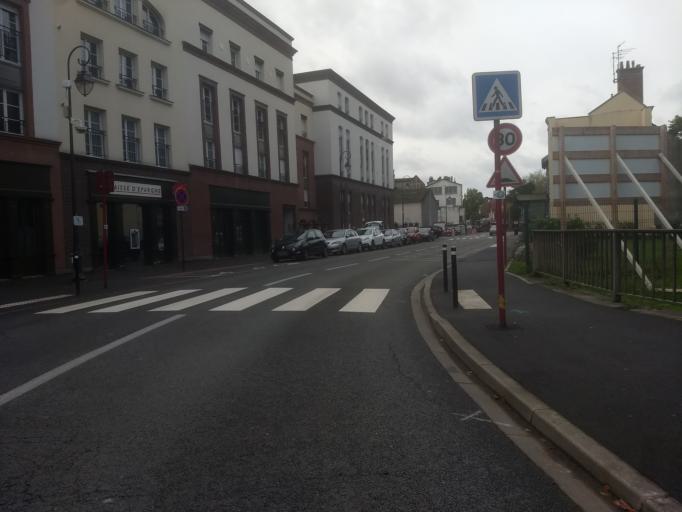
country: FR
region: Nord-Pas-de-Calais
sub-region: Departement du Pas-de-Calais
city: Saint-Nicolas
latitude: 50.3003
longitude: 2.7750
